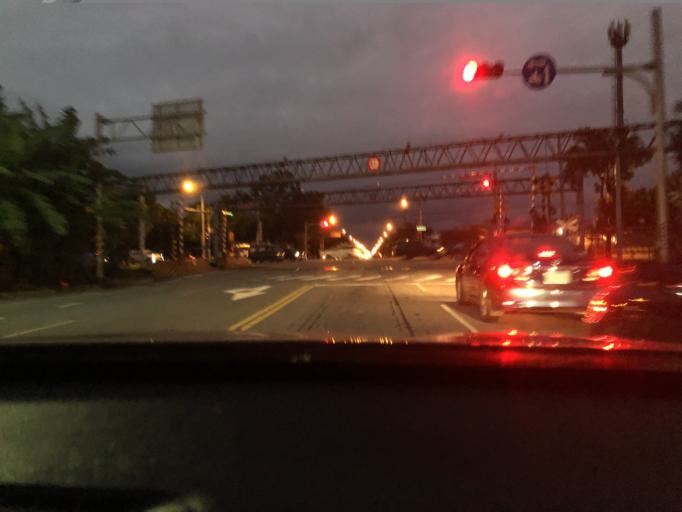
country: TW
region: Taiwan
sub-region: Hualien
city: Hualian
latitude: 23.9523
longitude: 121.5592
